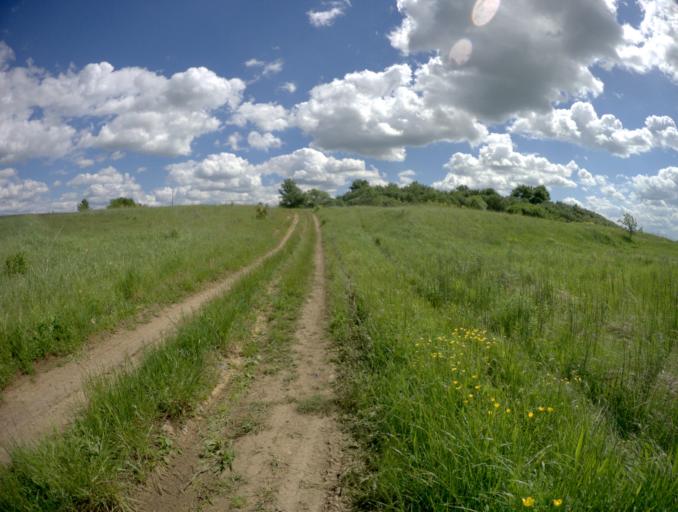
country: RU
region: Ivanovo
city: Gavrilov Posad
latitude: 56.4394
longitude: 40.2553
